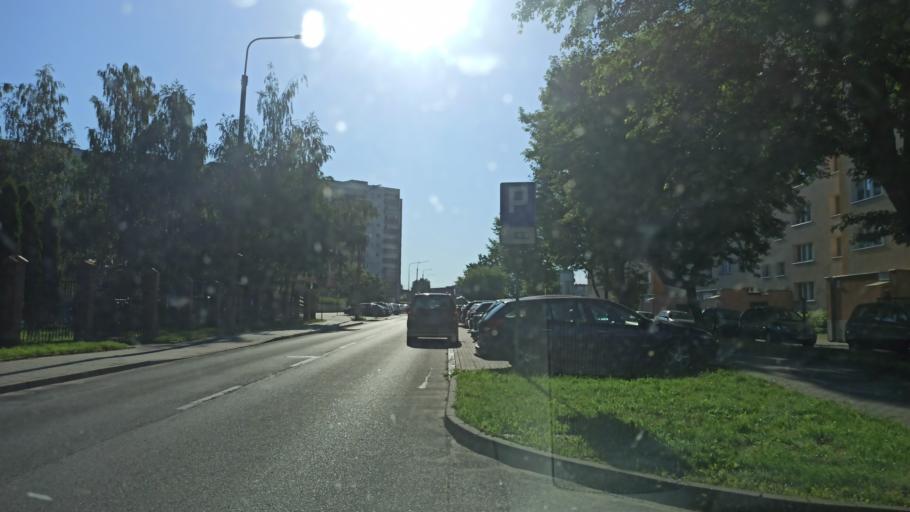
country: PL
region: Warmian-Masurian Voivodeship
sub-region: Powiat elblaski
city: Elblag
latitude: 54.1842
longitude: 19.3971
